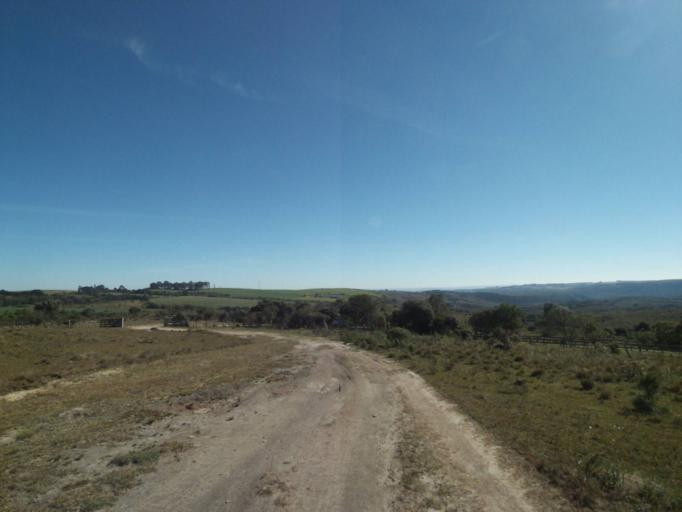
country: BR
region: Parana
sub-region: Tibagi
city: Tibagi
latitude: -24.5898
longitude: -50.2519
